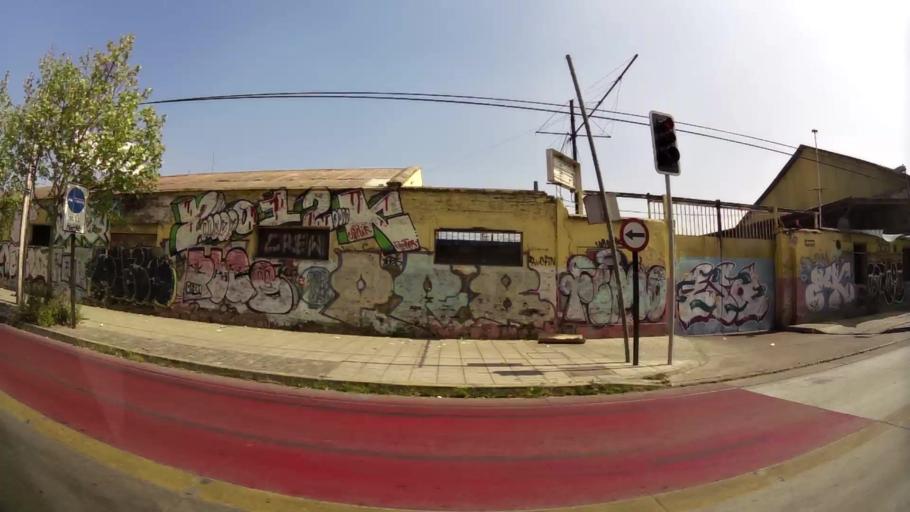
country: CL
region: Santiago Metropolitan
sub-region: Provincia de Santiago
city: Santiago
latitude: -33.4556
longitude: -70.6782
